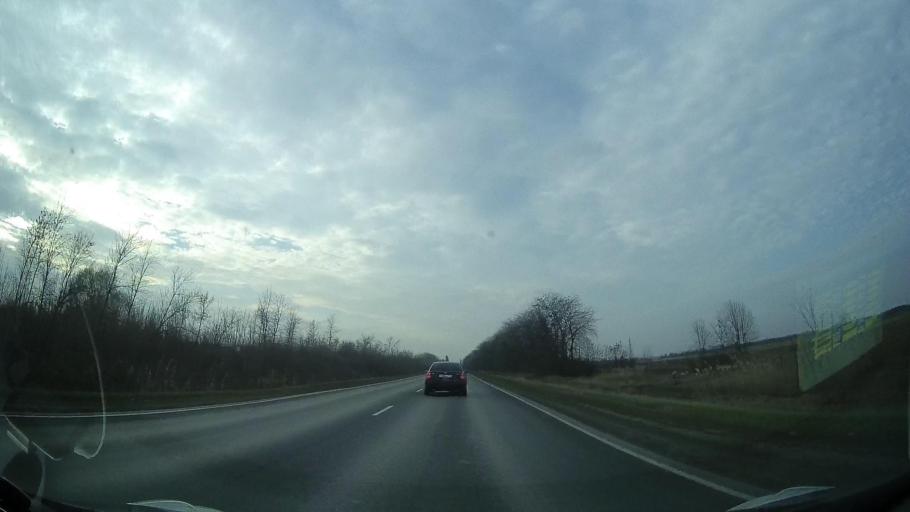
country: RU
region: Rostov
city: Ol'ginskaya
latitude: 47.1375
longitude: 40.0224
